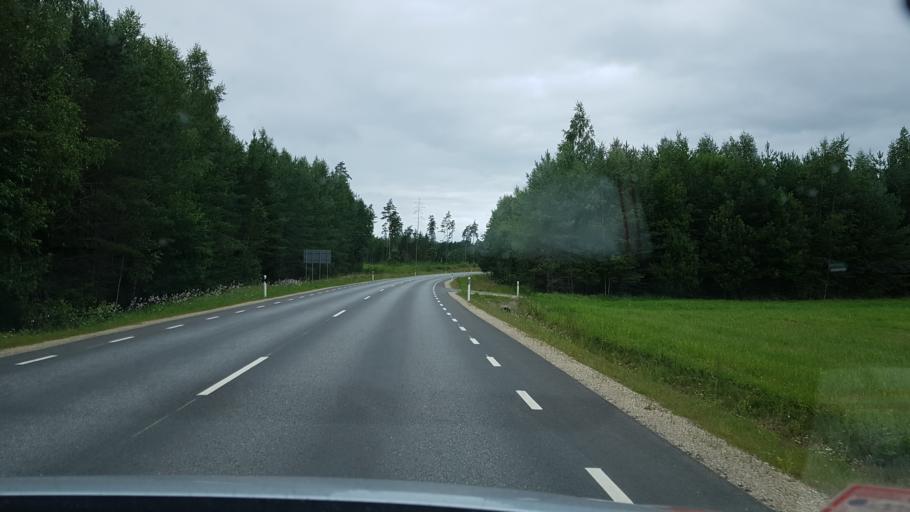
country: EE
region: Polvamaa
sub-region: Raepina vald
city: Rapina
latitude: 58.0716
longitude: 27.2695
